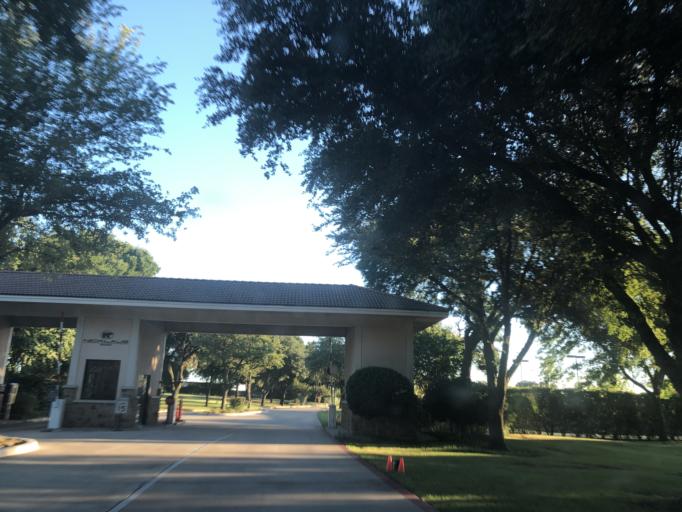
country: US
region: Texas
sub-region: Dallas County
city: Garland
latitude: 32.8383
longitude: -96.6456
